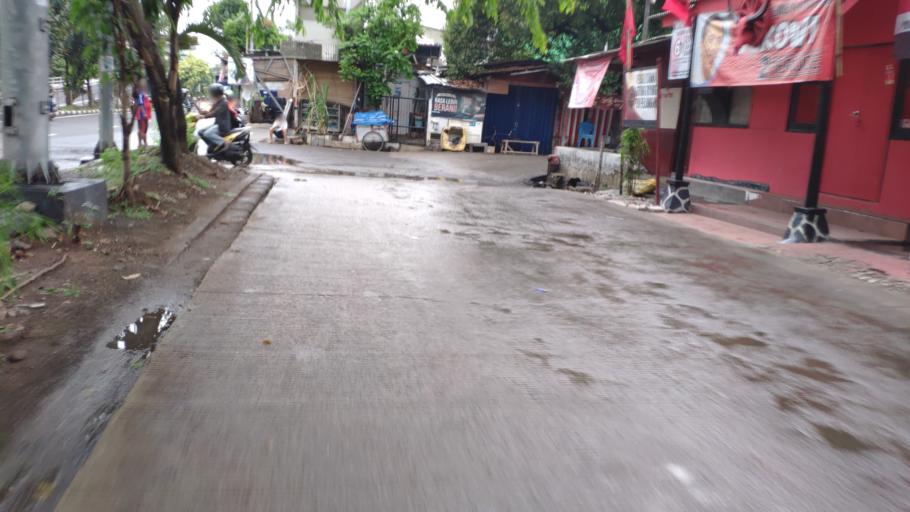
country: ID
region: Jakarta Raya
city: Jakarta
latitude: -6.2115
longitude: 106.8744
